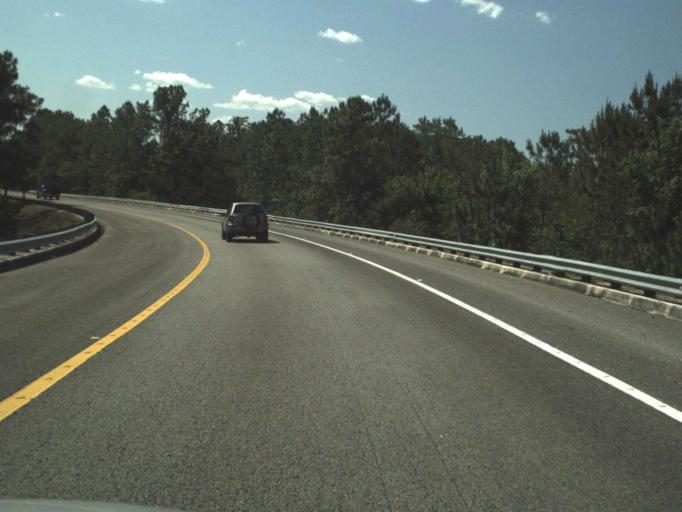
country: US
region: Florida
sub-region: Orange County
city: Bithlo
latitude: 28.5379
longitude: -81.0797
